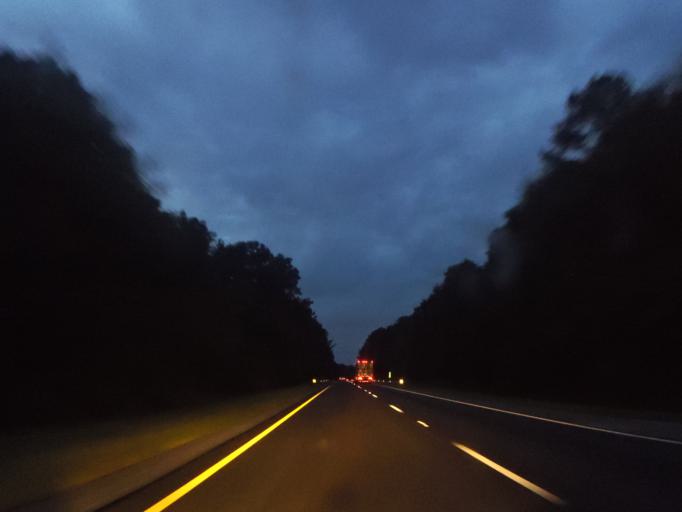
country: US
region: Alabama
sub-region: DeKalb County
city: Collinsville
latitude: 34.3094
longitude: -85.8541
